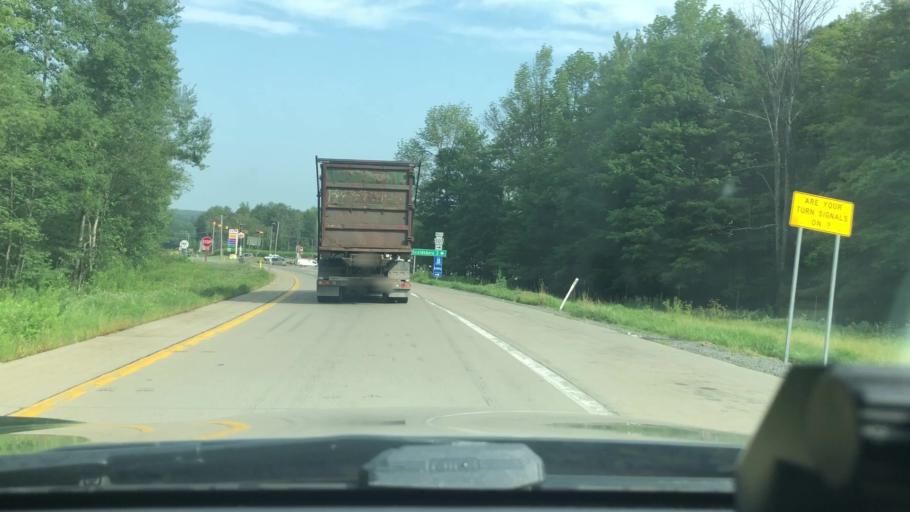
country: US
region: Pennsylvania
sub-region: Lackawanna County
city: Moscow
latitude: 41.2310
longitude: -75.4952
